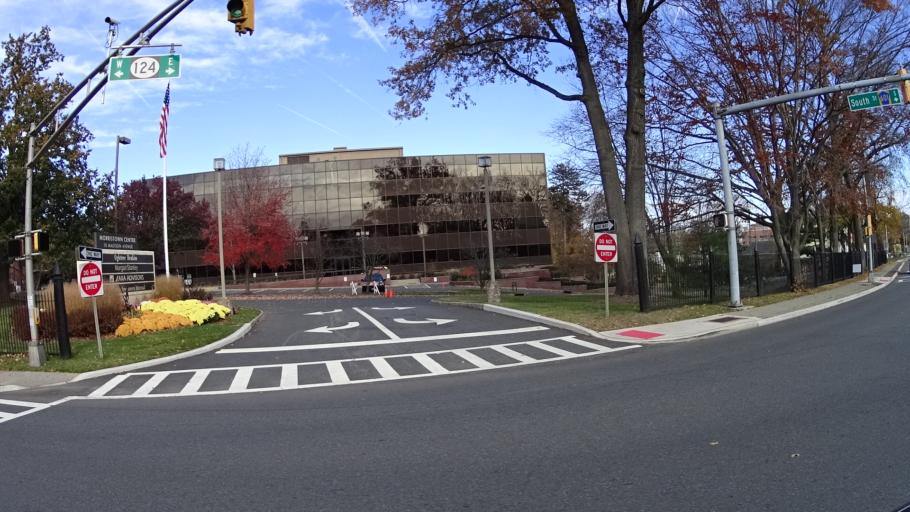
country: US
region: New Jersey
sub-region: Morris County
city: Morristown
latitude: 40.7888
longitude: -74.4722
